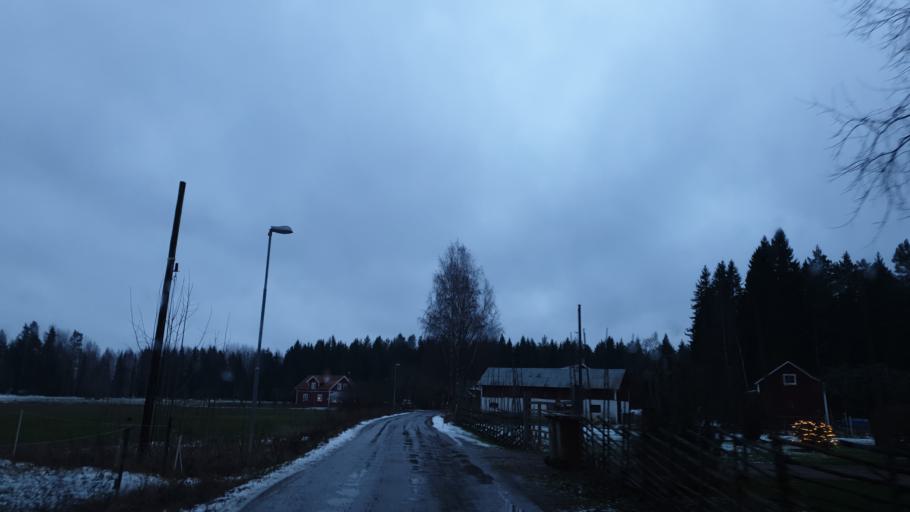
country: SE
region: Uppsala
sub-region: Tierps Kommun
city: Tierp
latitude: 60.3408
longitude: 17.4745
